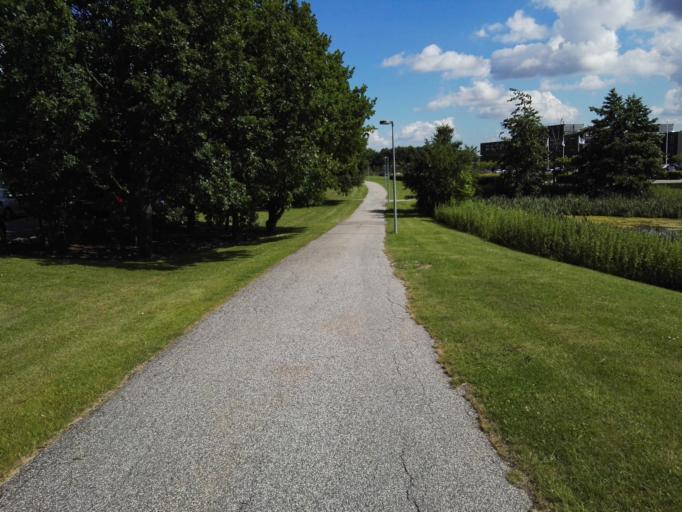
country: DK
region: Capital Region
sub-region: Ballerup Kommune
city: Ballerup
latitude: 55.7393
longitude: 12.3883
